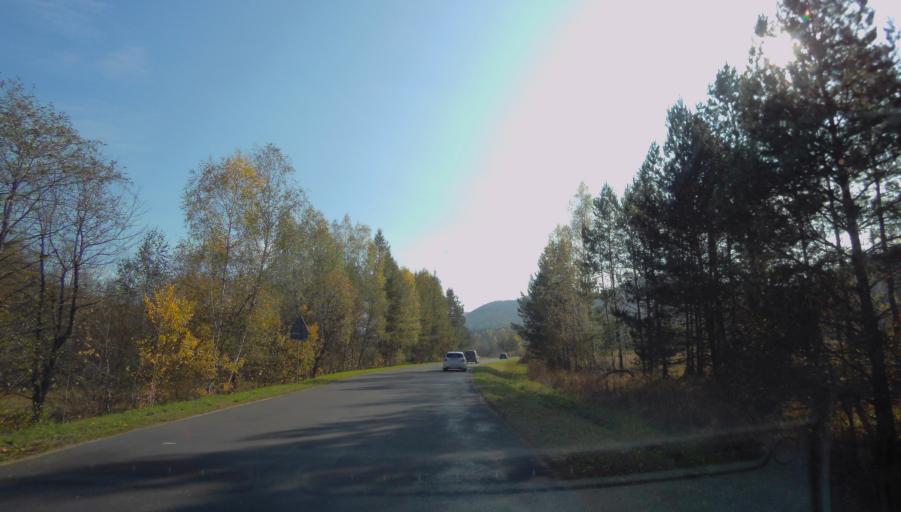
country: PL
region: Subcarpathian Voivodeship
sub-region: Powiat leski
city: Baligrod
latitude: 49.2256
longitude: 22.1773
